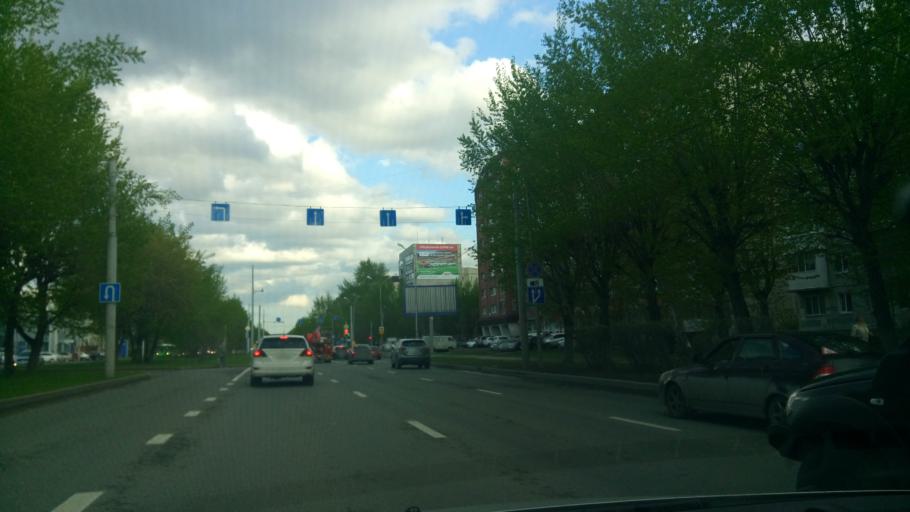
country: RU
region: Tjumen
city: Tyumen
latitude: 57.1393
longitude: 65.5934
